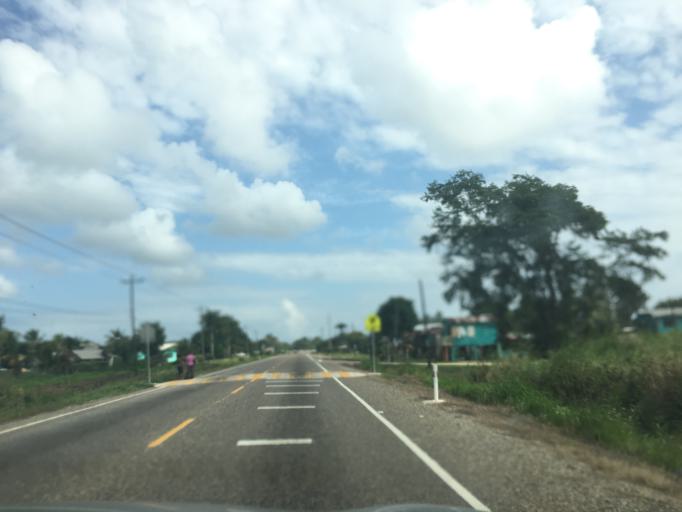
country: BZ
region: Stann Creek
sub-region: Dangriga
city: Dangriga
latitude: 16.9998
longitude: -88.3124
